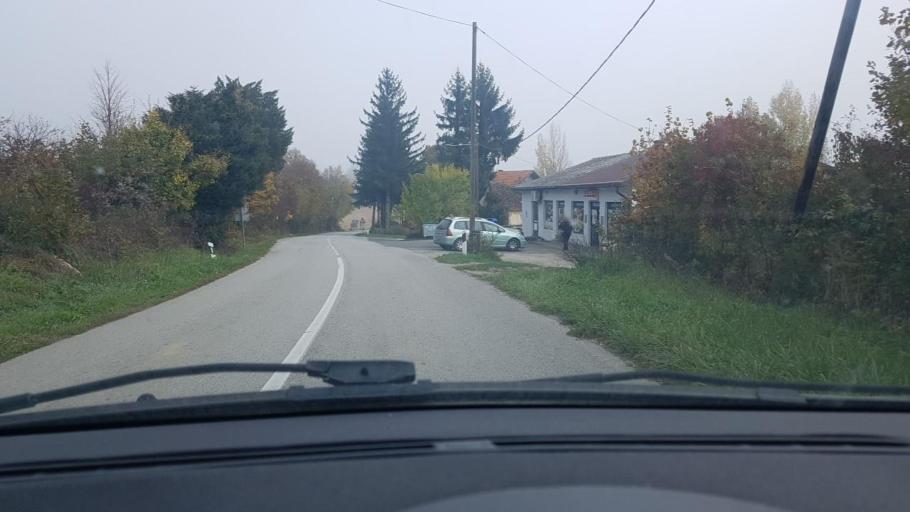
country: HR
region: Krapinsko-Zagorska
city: Zlatar
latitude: 46.1375
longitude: 16.1409
